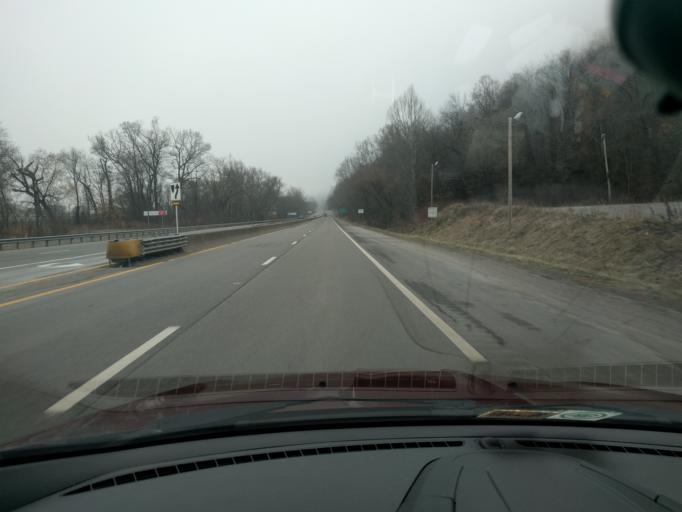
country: US
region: West Virginia
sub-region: Kanawha County
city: Rand
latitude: 38.2896
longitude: -81.5599
